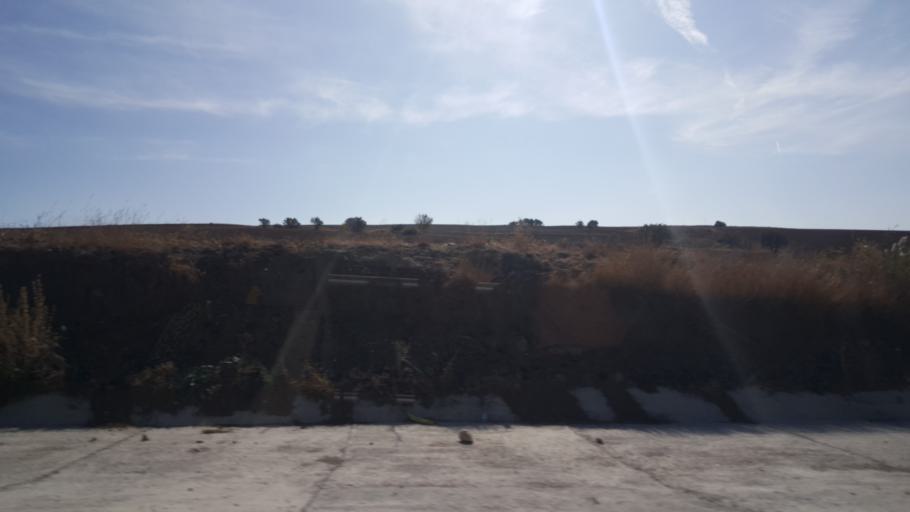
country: TR
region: Ankara
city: Haymana
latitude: 39.4019
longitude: 32.6210
